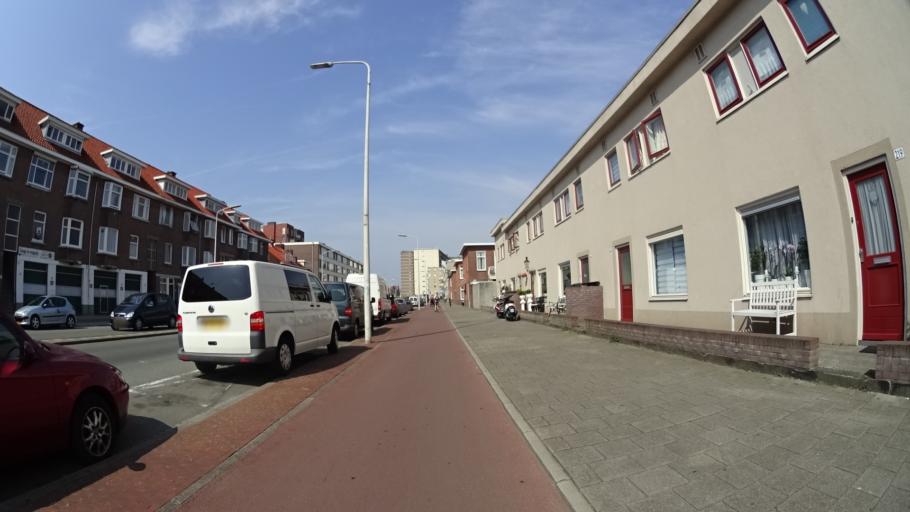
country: NL
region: South Holland
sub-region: Gemeente Den Haag
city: Scheveningen
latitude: 52.0976
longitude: 4.2715
